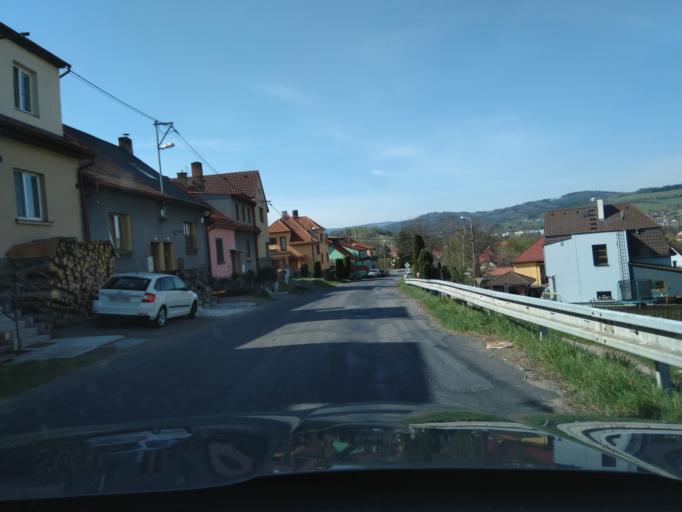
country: CZ
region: Plzensky
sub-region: Okres Klatovy
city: Susice
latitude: 49.2325
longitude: 13.5286
